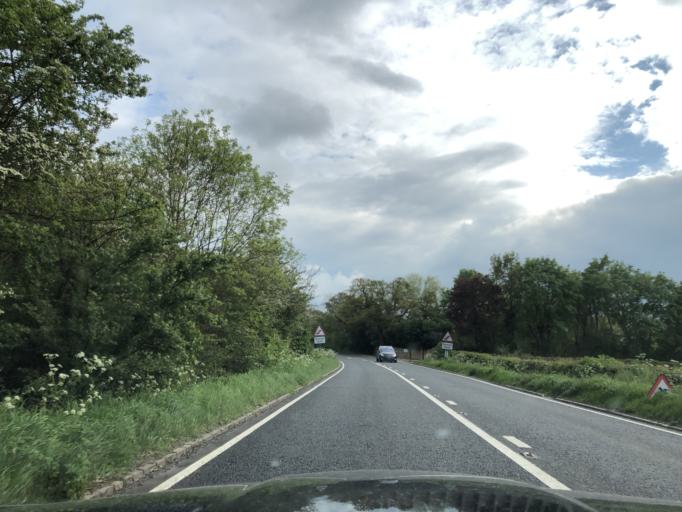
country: GB
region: England
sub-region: Gloucestershire
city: Moreton in Marsh
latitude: 51.9986
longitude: -1.6981
